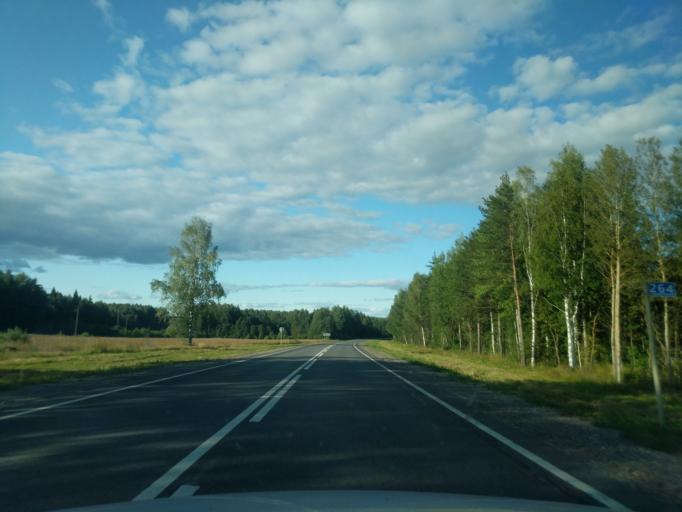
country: RU
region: Kostroma
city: Manturovo
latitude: 58.3392
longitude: 44.7170
